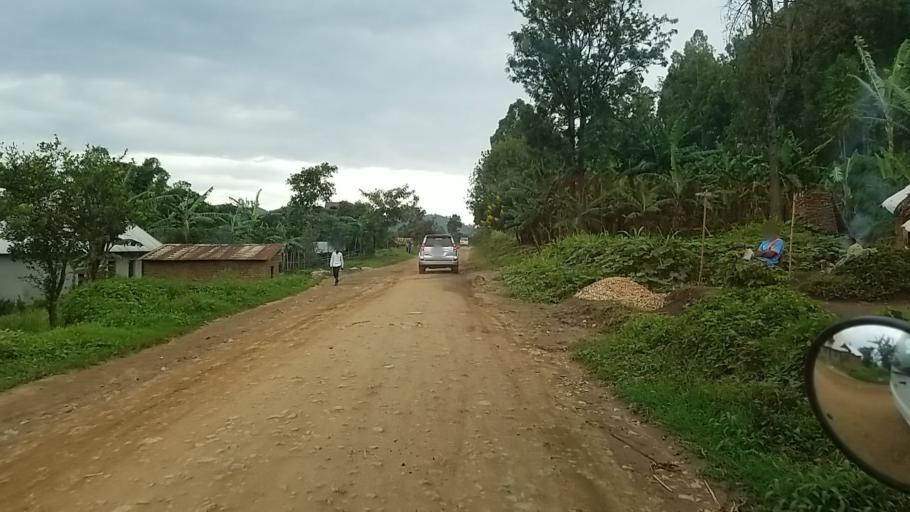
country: CD
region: Nord Kivu
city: Sake
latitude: -1.6720
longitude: 29.0175
